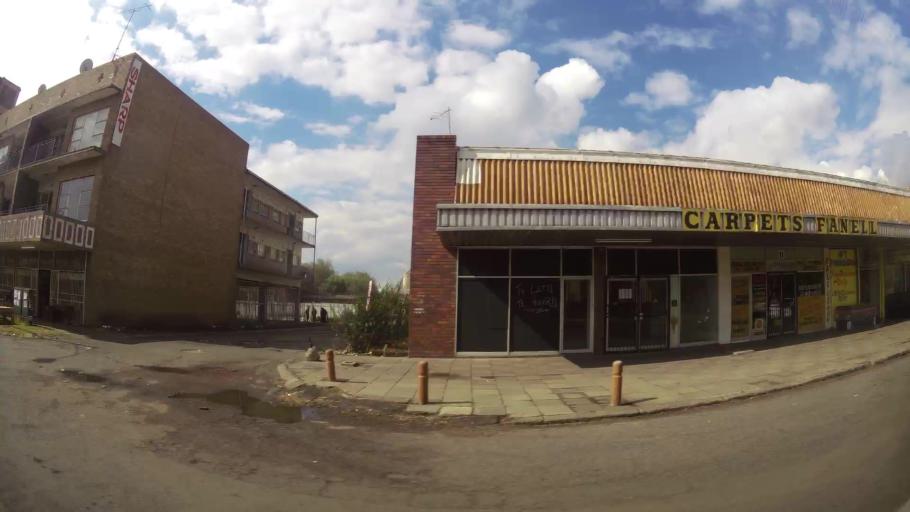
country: ZA
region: Gauteng
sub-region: Sedibeng District Municipality
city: Vereeniging
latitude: -26.6702
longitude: 27.9304
